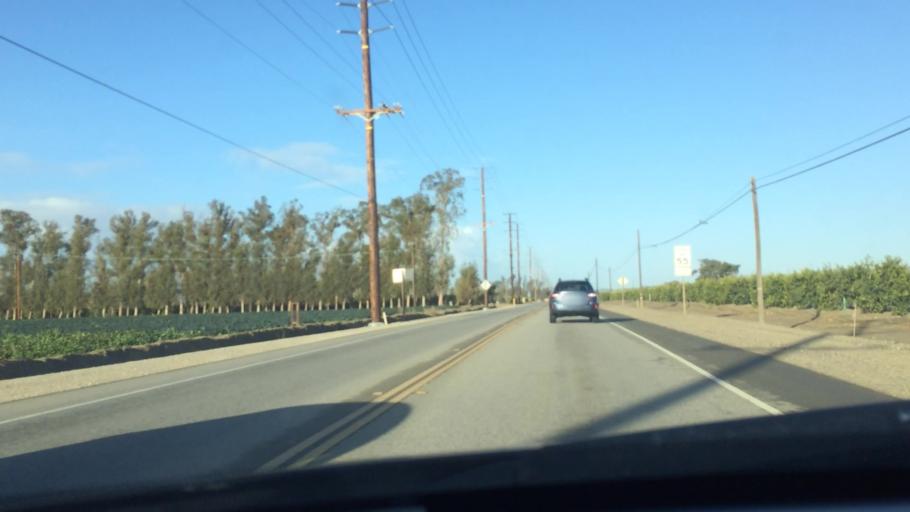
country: US
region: California
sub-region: Ventura County
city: Camarillo
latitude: 34.2637
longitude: -119.0784
